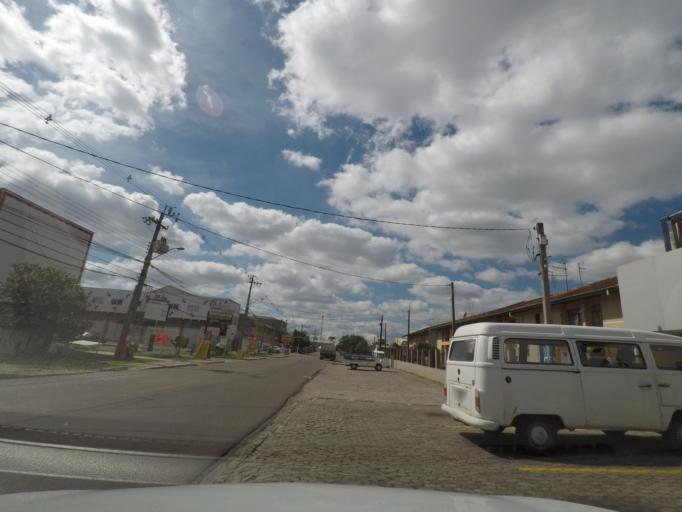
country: BR
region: Parana
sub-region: Sao Jose Dos Pinhais
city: Sao Jose dos Pinhais
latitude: -25.5051
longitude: -49.2200
